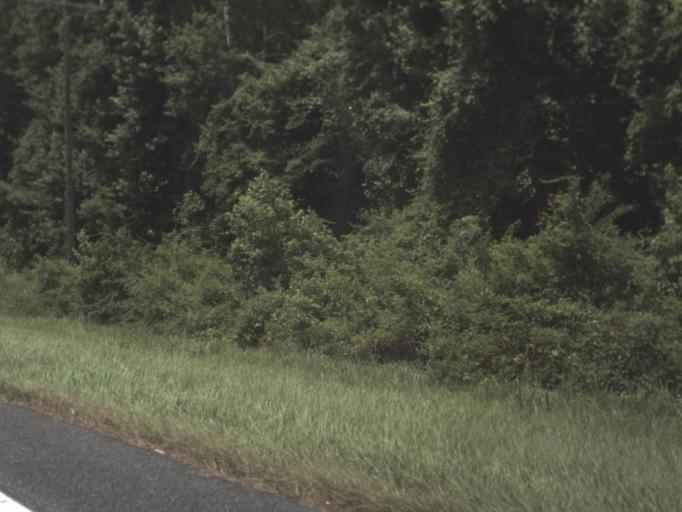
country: US
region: Florida
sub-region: Taylor County
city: Perry
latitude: 30.2861
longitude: -83.7324
